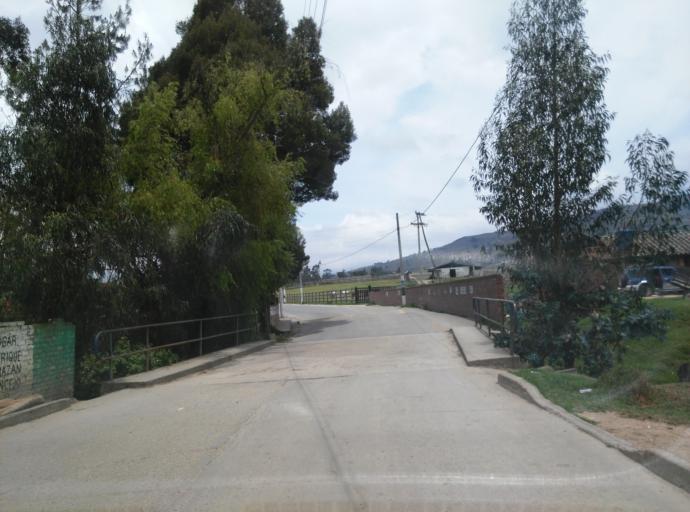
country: CO
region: Boyaca
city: Siachoque
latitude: 5.5111
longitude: -73.2469
